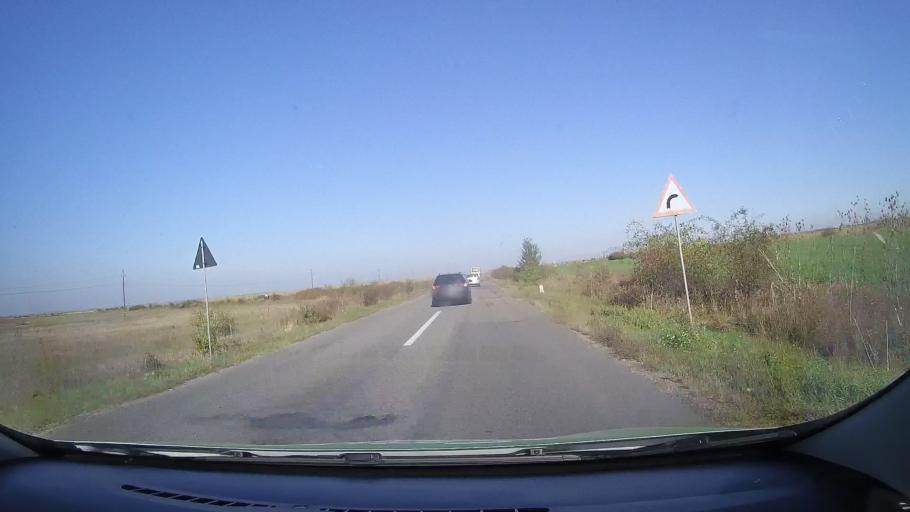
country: RO
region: Satu Mare
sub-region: Comuna Cauas
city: Cauas
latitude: 47.5778
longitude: 22.5493
